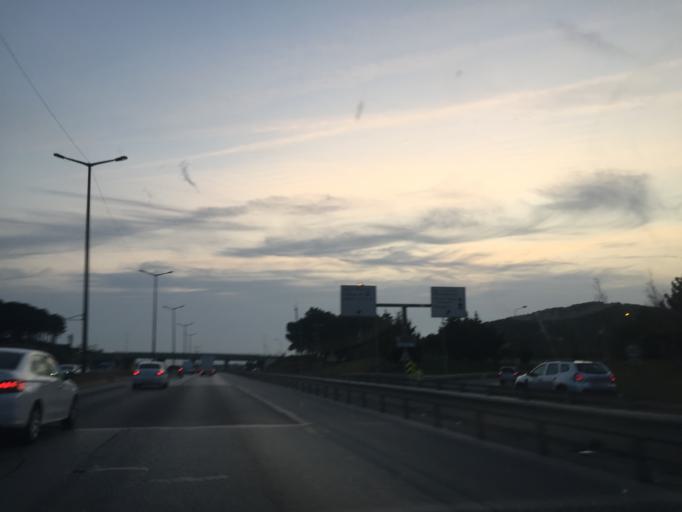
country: TR
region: Istanbul
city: Samandira
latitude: 40.9483
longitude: 29.2183
